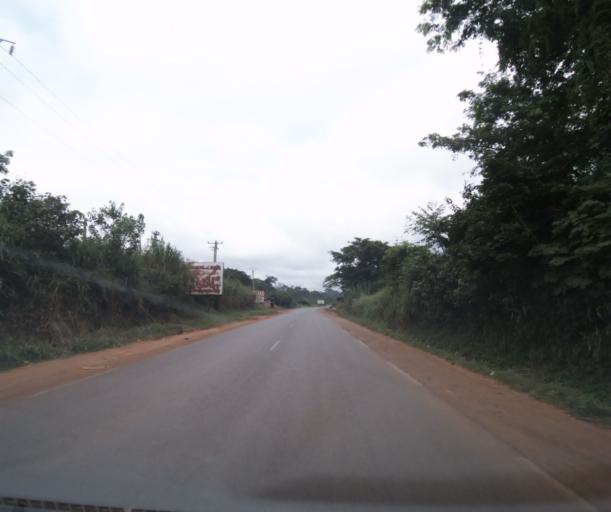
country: CM
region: Centre
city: Mbankomo
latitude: 3.7888
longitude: 11.4711
